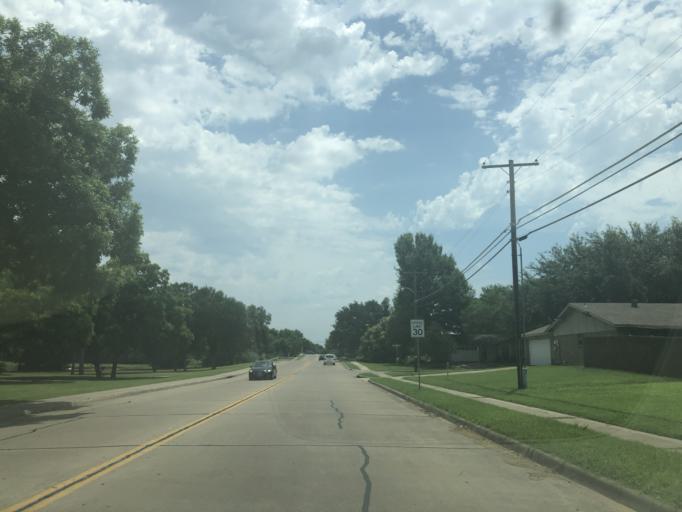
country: US
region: Texas
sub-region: Dallas County
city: Irving
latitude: 32.7939
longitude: -96.9379
